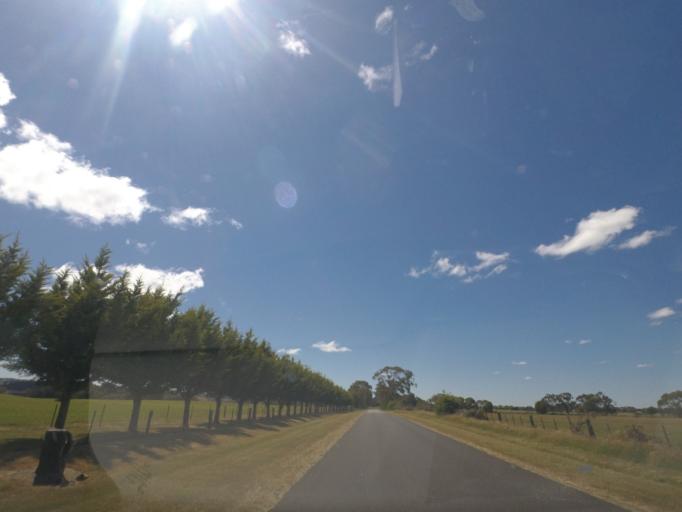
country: AU
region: Victoria
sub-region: Mount Alexander
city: Castlemaine
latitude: -37.3256
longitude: 144.4419
